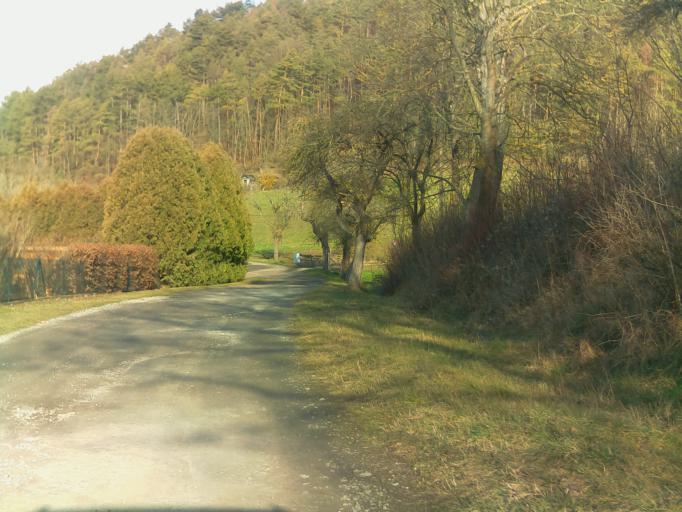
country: DE
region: Thuringia
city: Nauendorf
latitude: 50.8962
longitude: 11.1827
